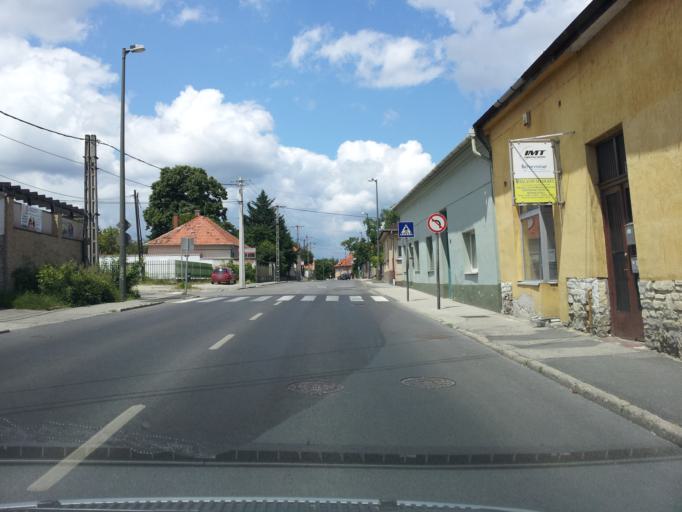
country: HU
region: Veszprem
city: Veszprem
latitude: 47.0923
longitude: 17.9027
